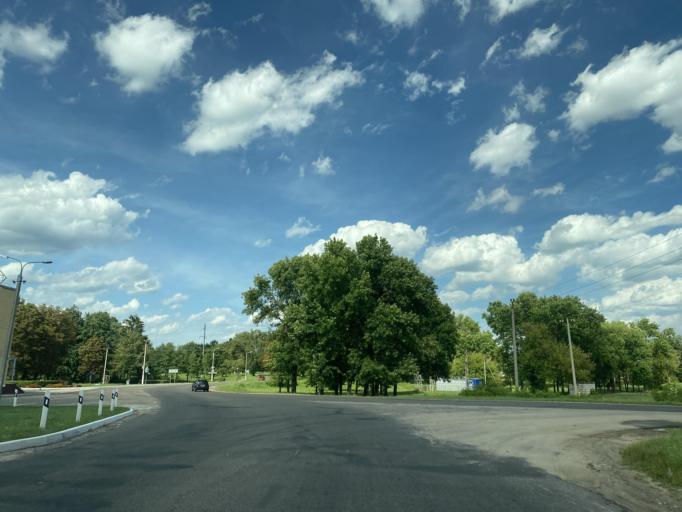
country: BY
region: Minsk
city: Horad Zhodzina
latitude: 54.0951
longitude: 28.3543
